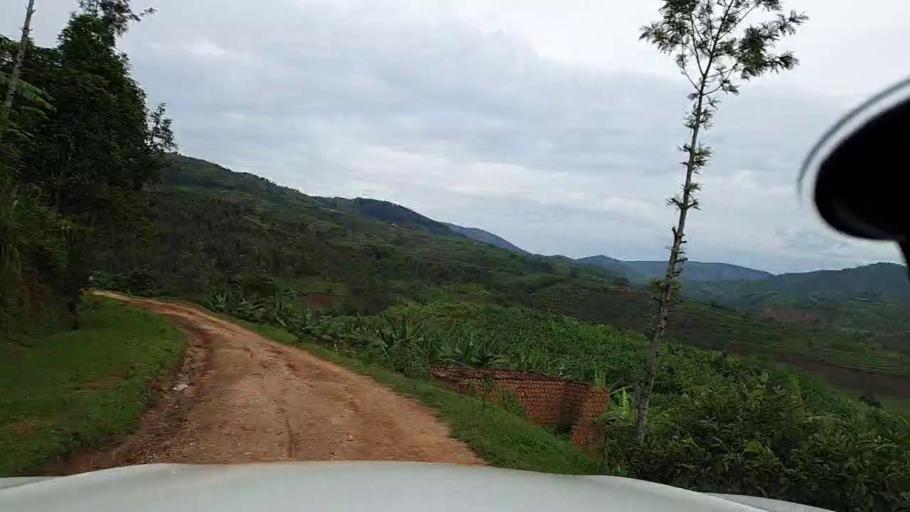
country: RW
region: Southern Province
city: Gitarama
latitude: -2.0920
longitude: 29.6374
